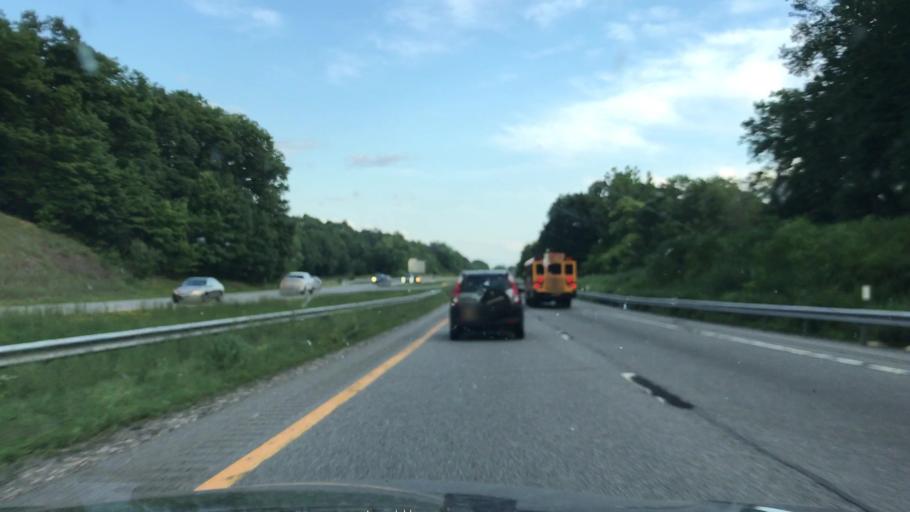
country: US
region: New York
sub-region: Orange County
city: Washington Heights
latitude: 41.5402
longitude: -74.4224
